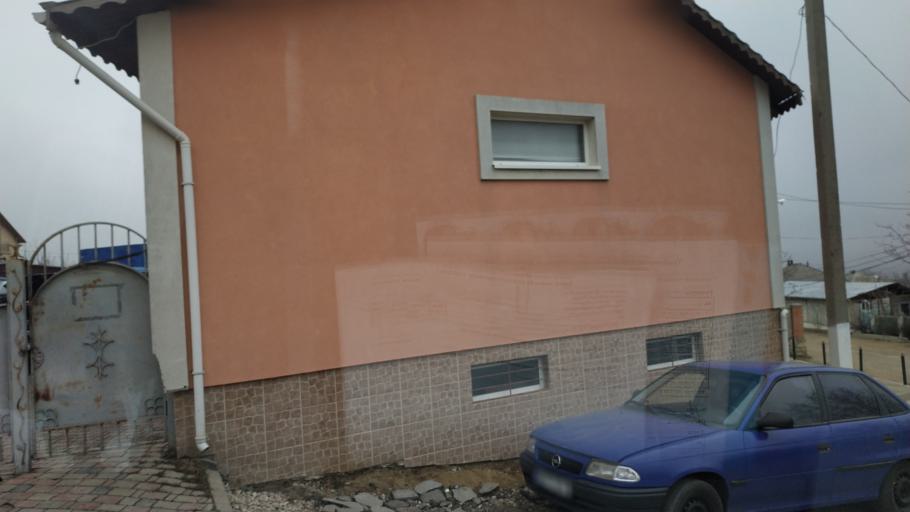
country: MD
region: Hincesti
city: Hincesti
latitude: 46.9090
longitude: 28.6671
